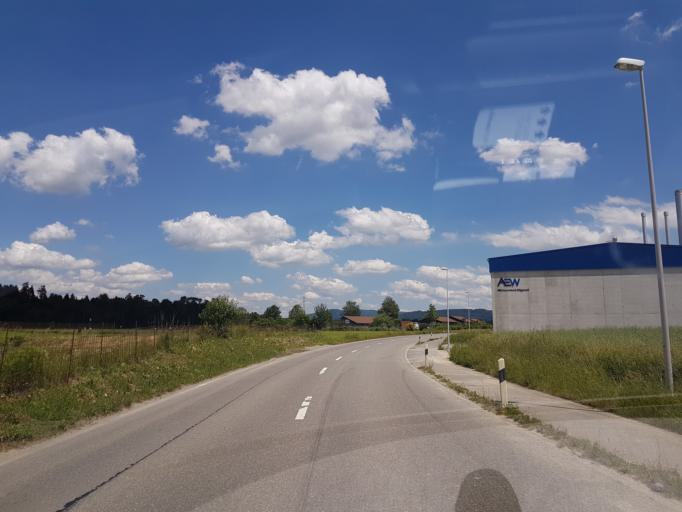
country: CH
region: Aargau
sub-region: Bezirk Lenzburg
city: Othmarsingen
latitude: 47.4154
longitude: 8.2269
